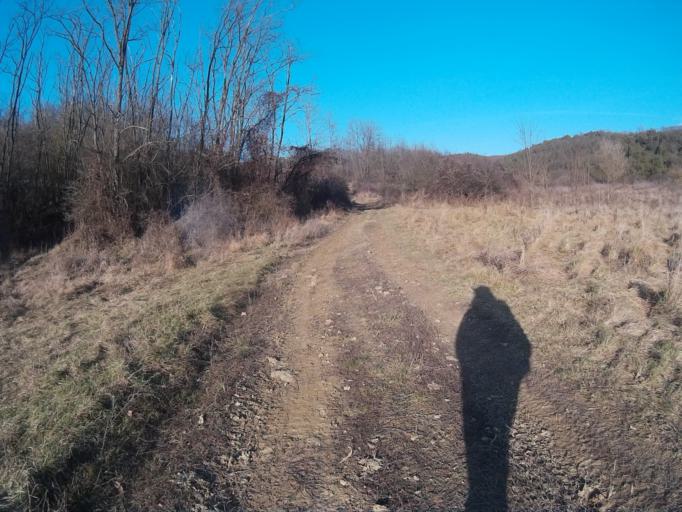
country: HU
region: Nograd
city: Bercel
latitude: 47.9575
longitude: 19.4402
